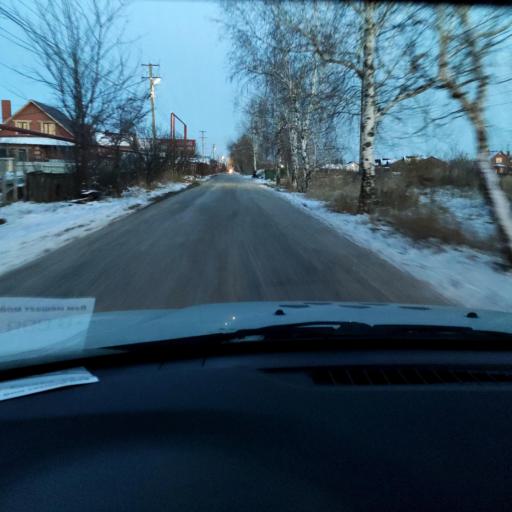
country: RU
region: Samara
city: Tol'yatti
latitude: 53.5608
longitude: 49.3807
